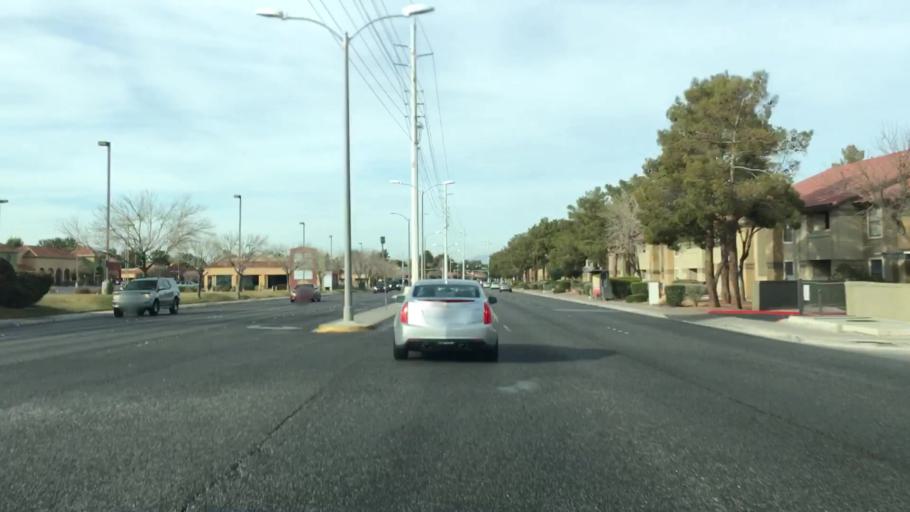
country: US
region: Nevada
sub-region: Clark County
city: Whitney
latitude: 36.0539
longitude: -115.0828
